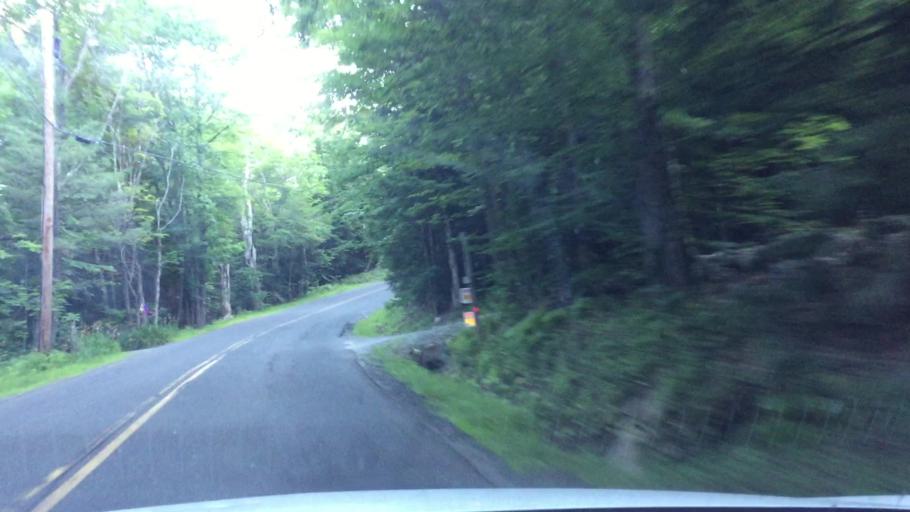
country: US
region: Massachusetts
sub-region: Berkshire County
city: Otis
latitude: 42.2426
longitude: -73.1126
